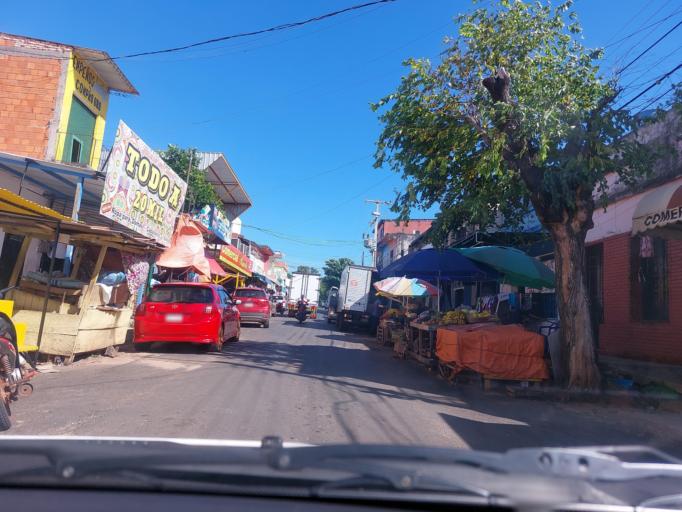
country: PY
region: San Pedro
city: Guayaybi
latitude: -24.6631
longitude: -56.4451
